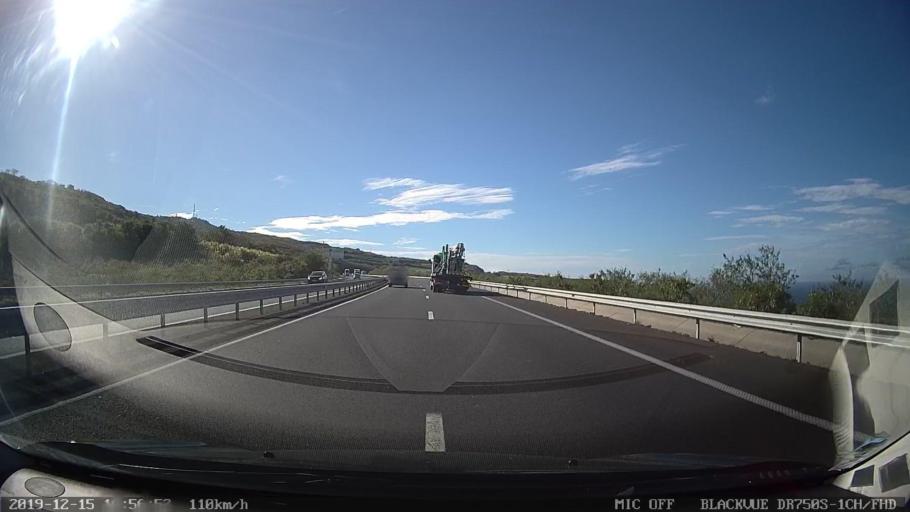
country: RE
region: Reunion
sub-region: Reunion
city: Trois-Bassins
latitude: -21.0770
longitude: 55.2524
